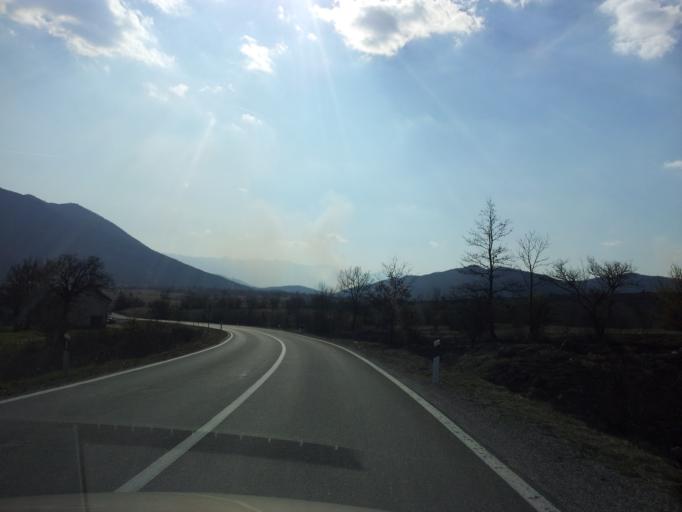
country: HR
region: Zadarska
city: Gracac
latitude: 44.4797
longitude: 15.7273
